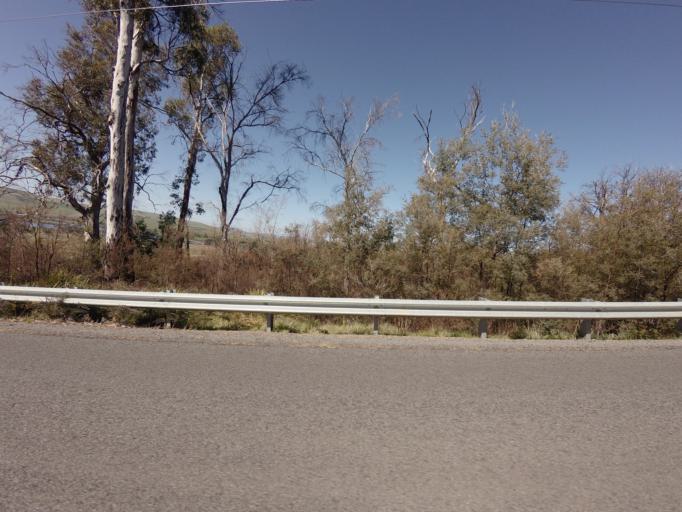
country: AU
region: Tasmania
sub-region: Derwent Valley
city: New Norfolk
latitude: -42.5402
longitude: 146.7206
